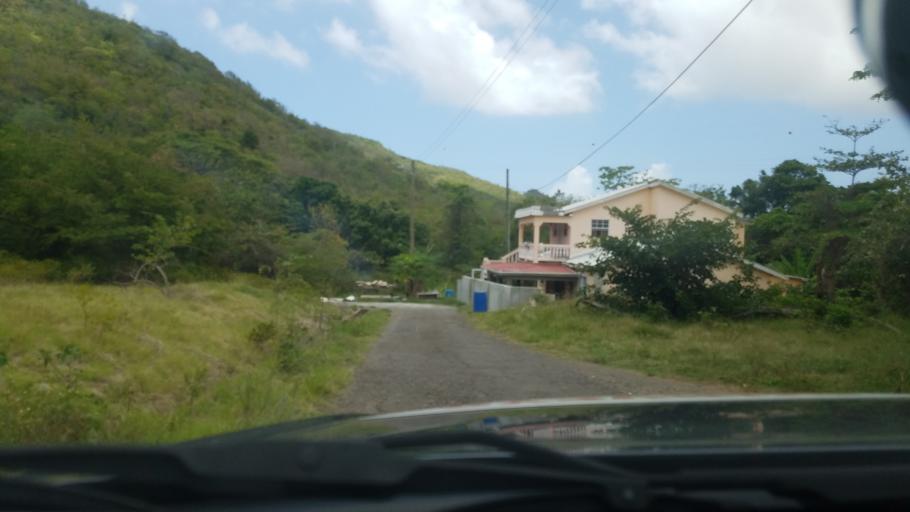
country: LC
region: Gros-Islet
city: Gros Islet
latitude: 14.0568
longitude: -60.9284
